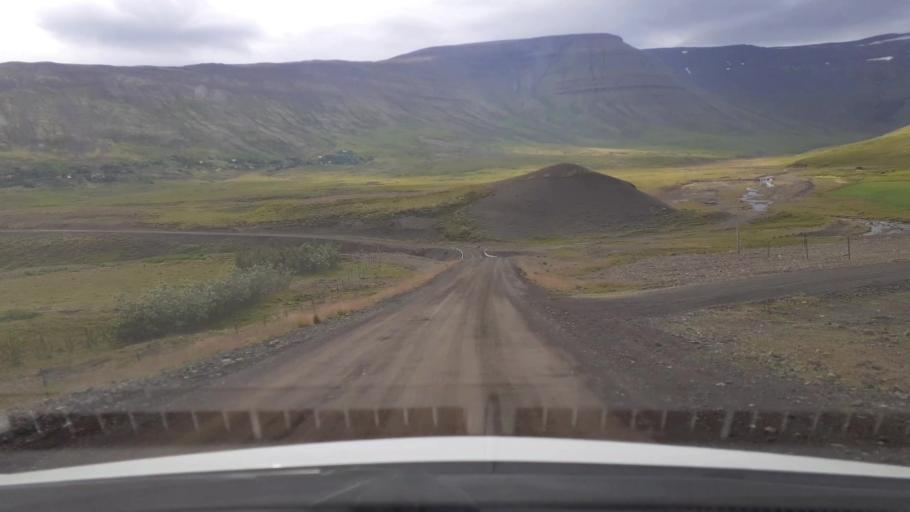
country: IS
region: Capital Region
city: Mosfellsbaer
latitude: 64.2959
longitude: -21.6638
